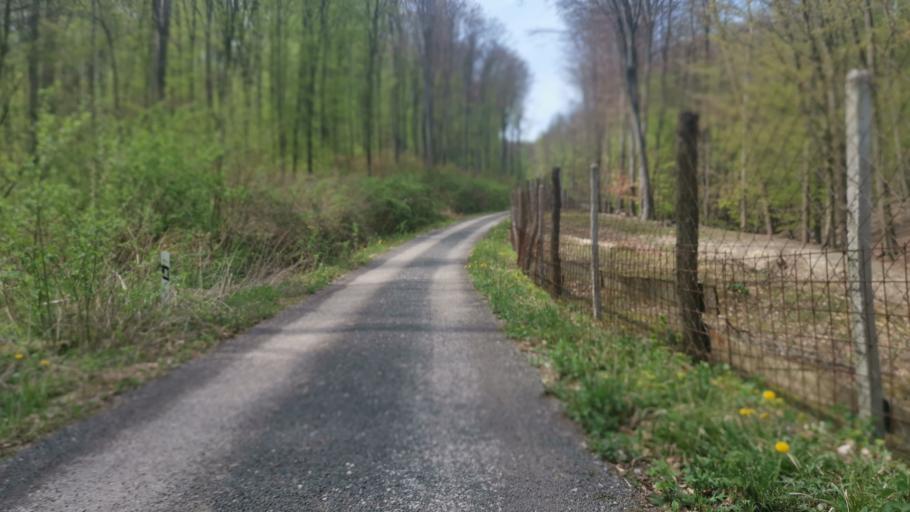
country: SK
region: Trnavsky
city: Smolenice
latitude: 48.5549
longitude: 17.4474
